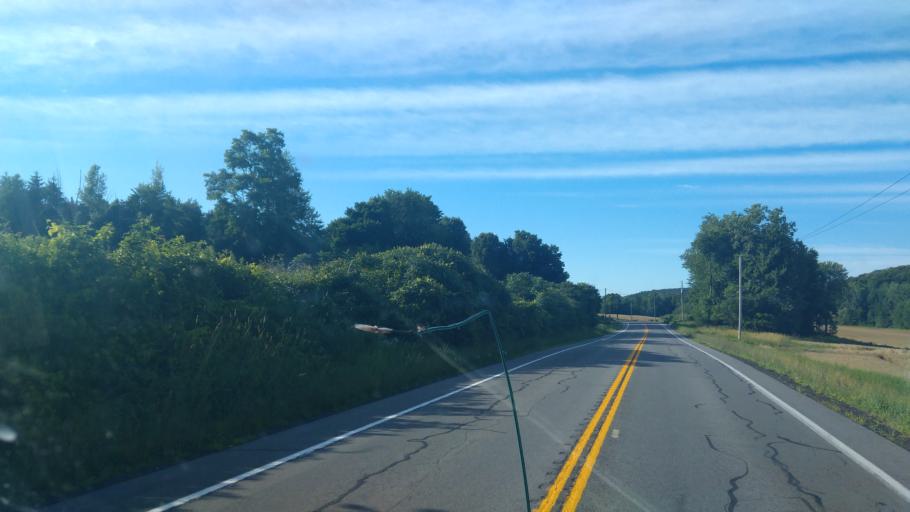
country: US
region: New York
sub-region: Wayne County
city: Lyons
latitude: 43.0958
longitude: -76.9842
